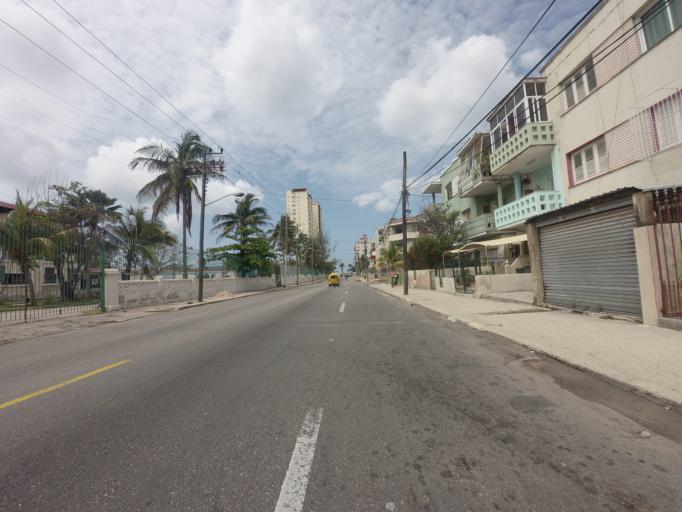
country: CU
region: La Habana
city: Havana
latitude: 23.1345
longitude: -82.4061
